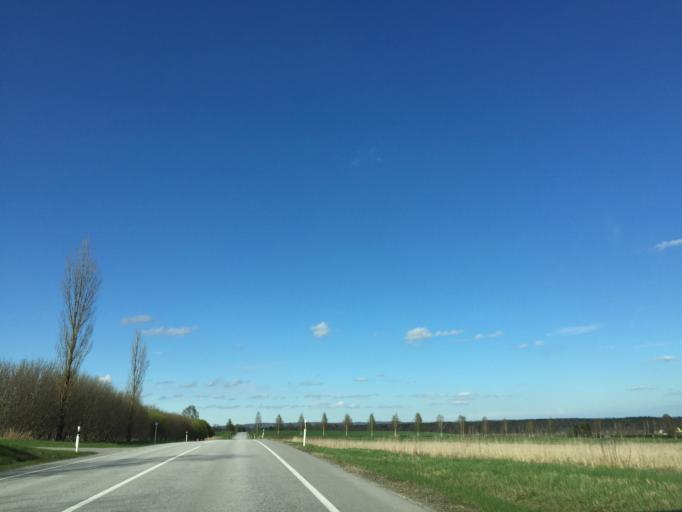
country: EE
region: Valgamaa
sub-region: Valga linn
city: Valga
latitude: 57.8757
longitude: 26.2778
